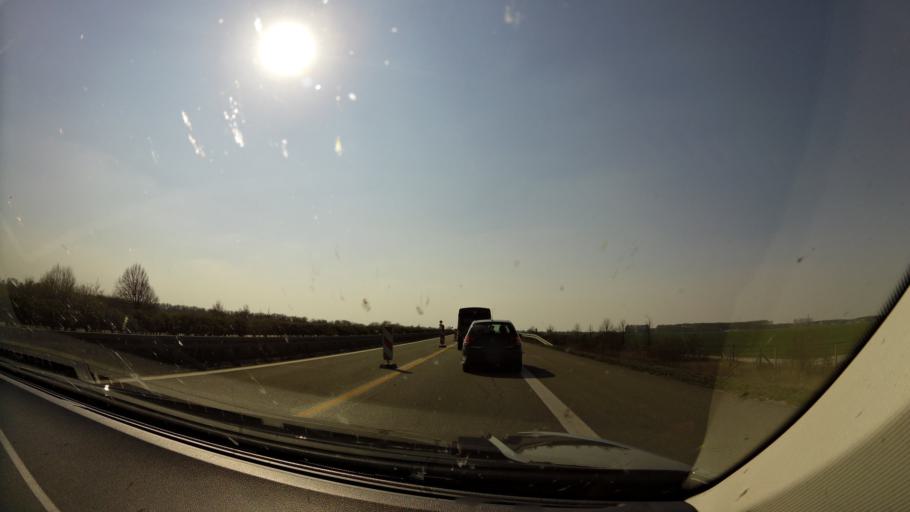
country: DE
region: Mecklenburg-Vorpommern
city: Grimmen
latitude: 54.0883
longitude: 12.9631
